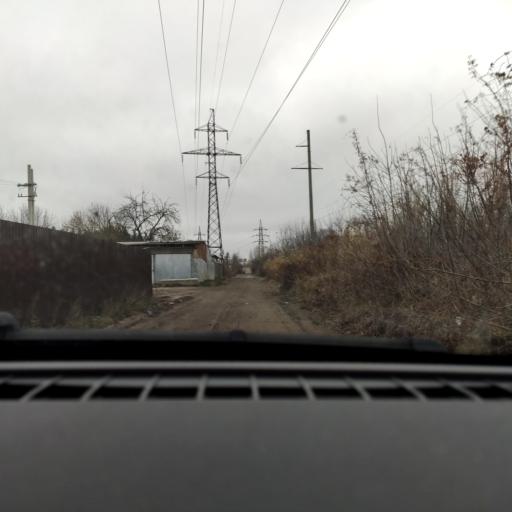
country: RU
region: Voronezj
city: Maslovka
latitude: 51.6045
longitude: 39.2706
